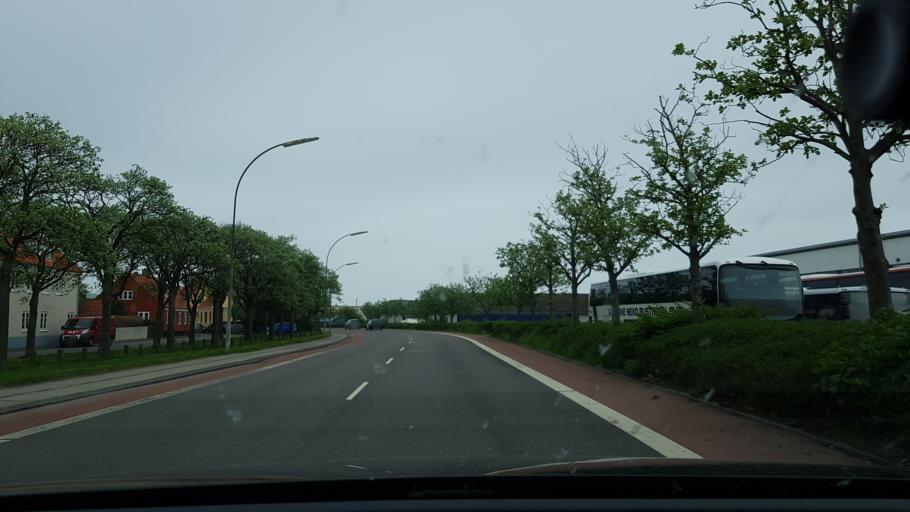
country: DK
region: Capital Region
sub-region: Bornholm Kommune
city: Nexo
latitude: 55.0581
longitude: 15.1305
